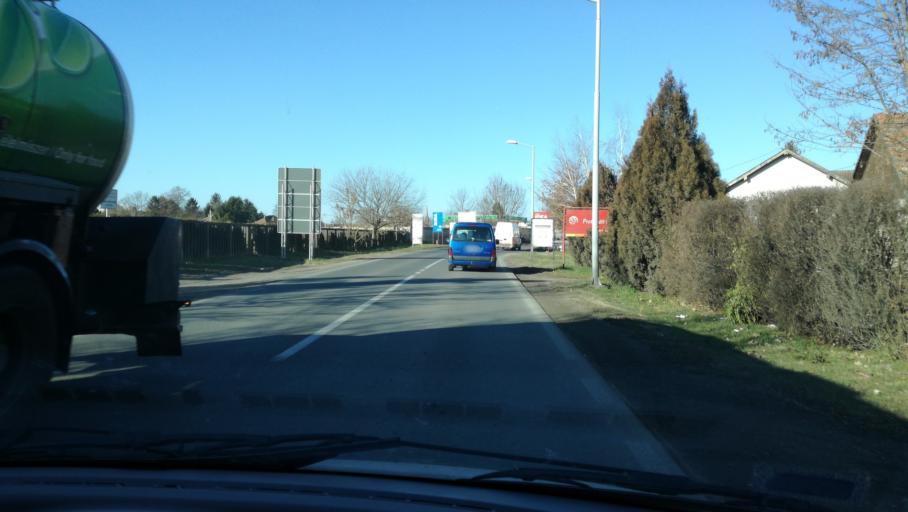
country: RS
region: Autonomna Pokrajina Vojvodina
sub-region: Severnobacki Okrug
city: Subotica
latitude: 46.0863
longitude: 19.6860
